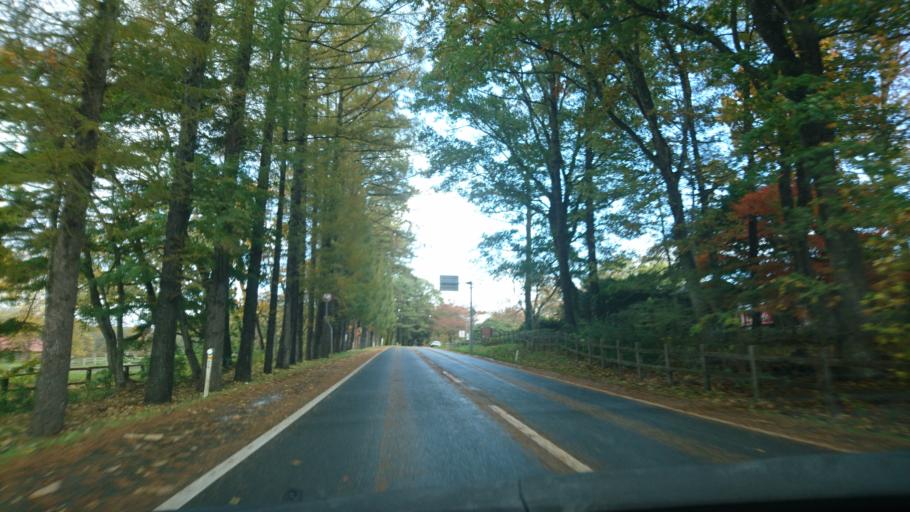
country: JP
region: Iwate
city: Shizukuishi
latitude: 39.7516
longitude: 141.0147
